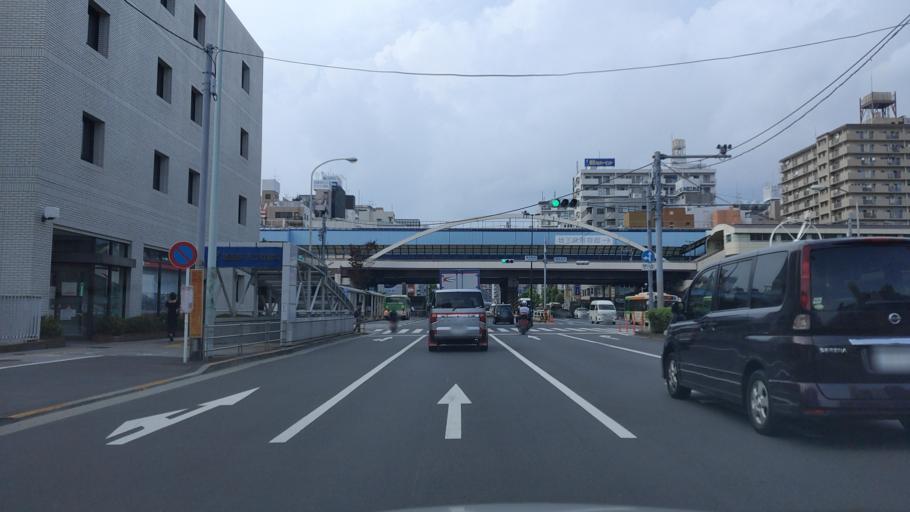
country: JP
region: Tokyo
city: Urayasu
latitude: 35.6625
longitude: 139.8730
